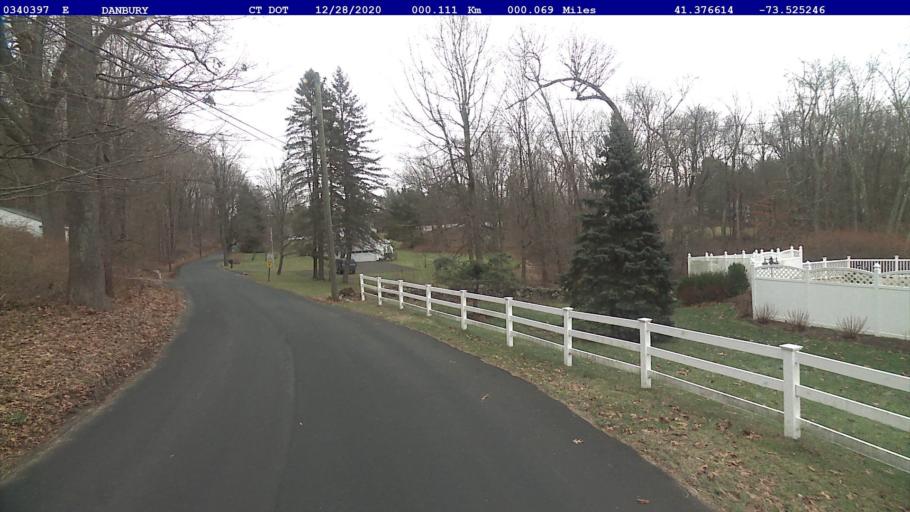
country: US
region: New York
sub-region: Putnam County
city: Peach Lake
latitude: 41.3766
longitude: -73.5252
